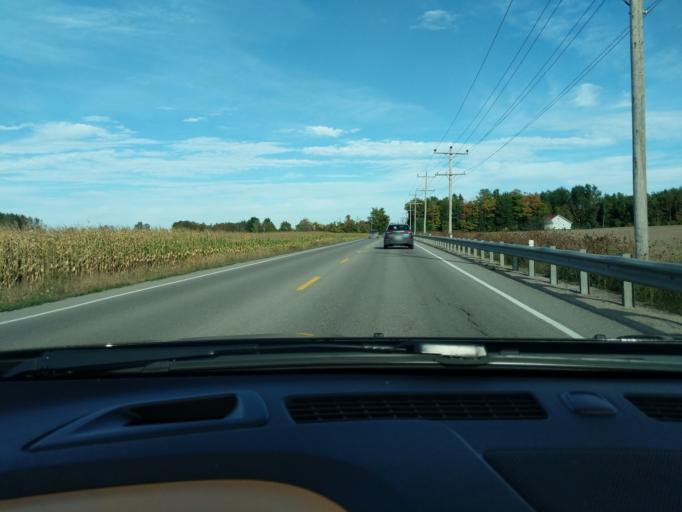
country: CA
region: Ontario
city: Wasaga Beach
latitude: 44.4355
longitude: -80.0960
